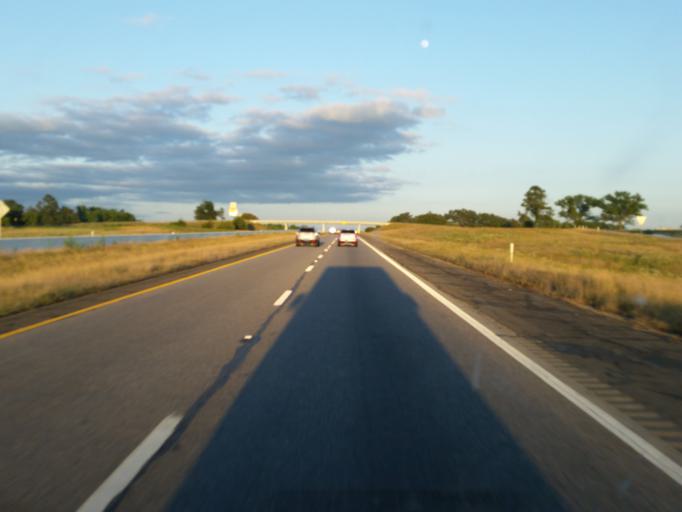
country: US
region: Texas
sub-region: Van Zandt County
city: Canton
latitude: 32.5438
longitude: -95.7612
